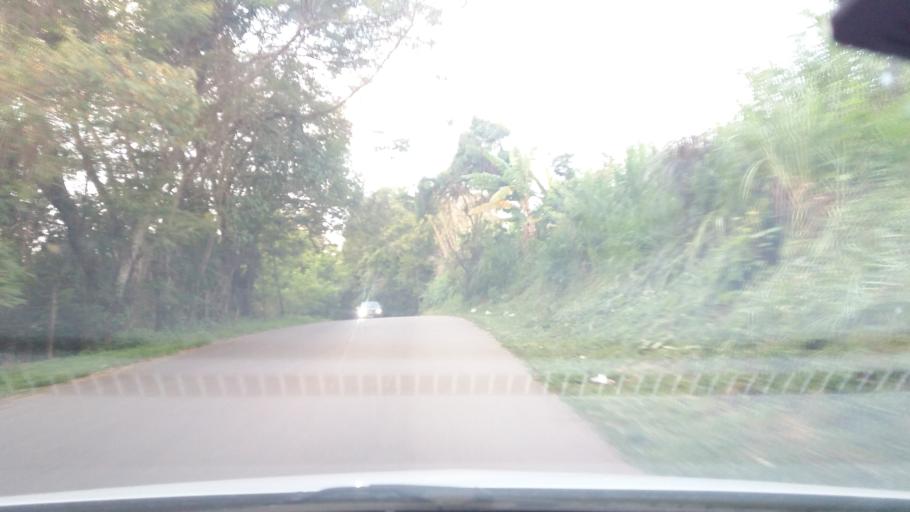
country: BR
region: Sao Paulo
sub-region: Bom Jesus Dos Perdoes
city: Bom Jesus dos Perdoes
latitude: -23.1679
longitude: -46.4783
